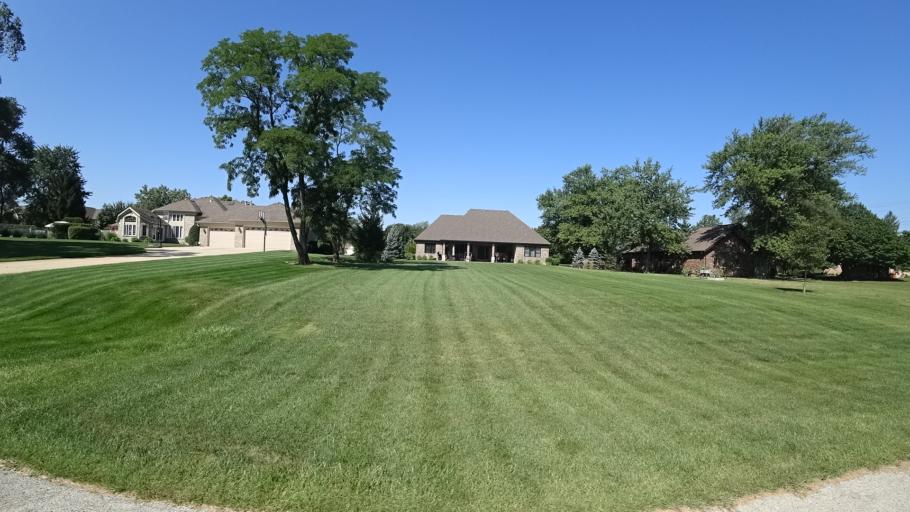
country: US
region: Illinois
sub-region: Cook County
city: Palos Heights
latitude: 41.6368
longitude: -87.8109
